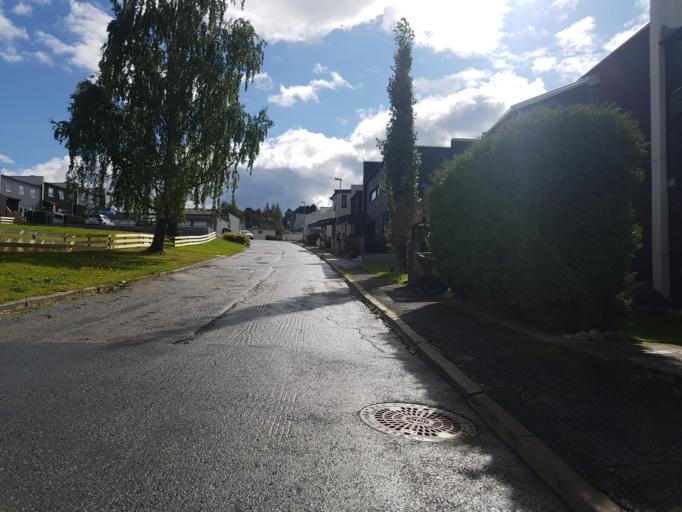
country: NO
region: Sor-Trondelag
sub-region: Trondheim
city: Trondheim
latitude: 63.4137
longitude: 10.4618
